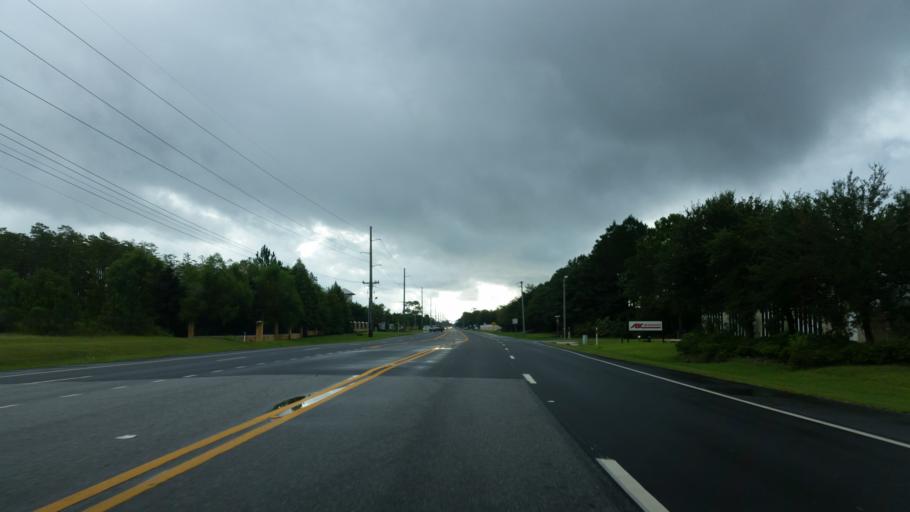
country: US
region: Alabama
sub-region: Baldwin County
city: Orange Beach
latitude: 30.2902
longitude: -87.6206
